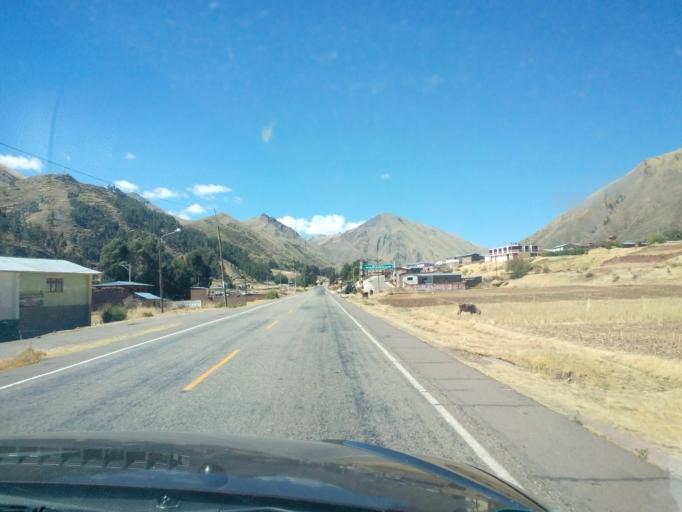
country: PE
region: Cusco
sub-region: Provincia de Canchis
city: Marangani
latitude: -14.3512
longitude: -71.1747
